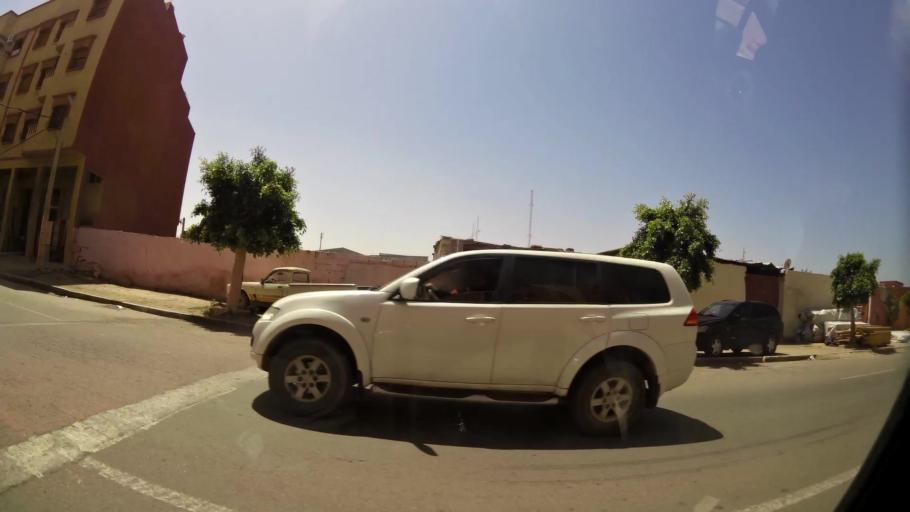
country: MA
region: Souss-Massa-Draa
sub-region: Inezgane-Ait Mellou
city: Inezgane
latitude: 30.3333
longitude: -9.5013
